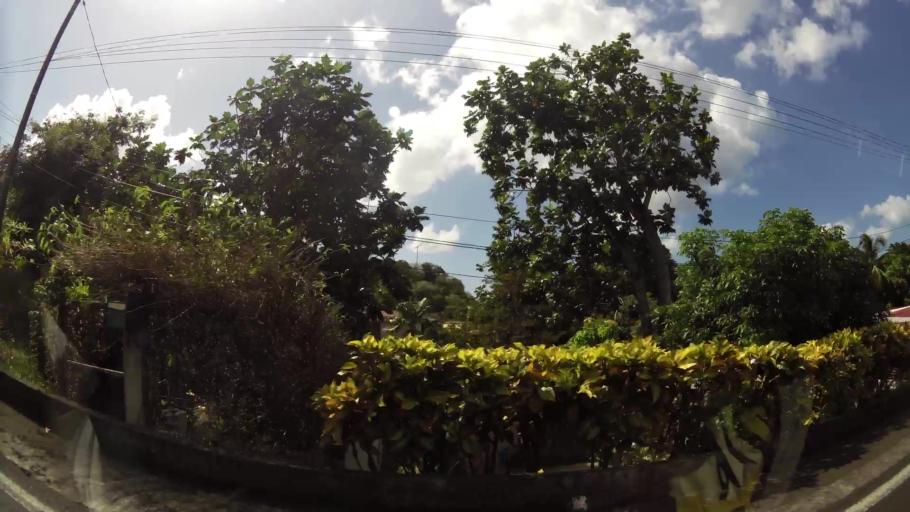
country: MQ
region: Martinique
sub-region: Martinique
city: Fort-de-France
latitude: 14.6421
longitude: -61.1361
